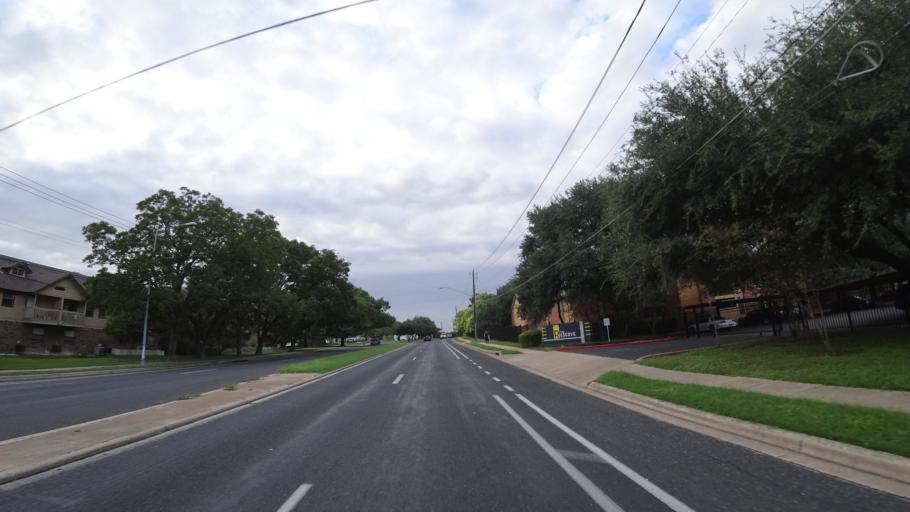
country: US
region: Texas
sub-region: Travis County
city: Rollingwood
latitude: 30.2095
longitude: -97.7847
